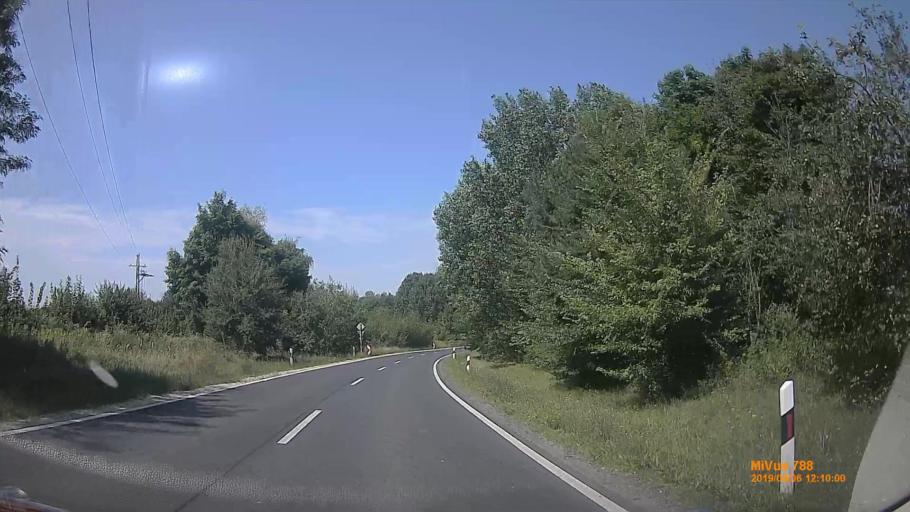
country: HU
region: Vas
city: Vasvar
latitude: 47.1007
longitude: 16.8771
